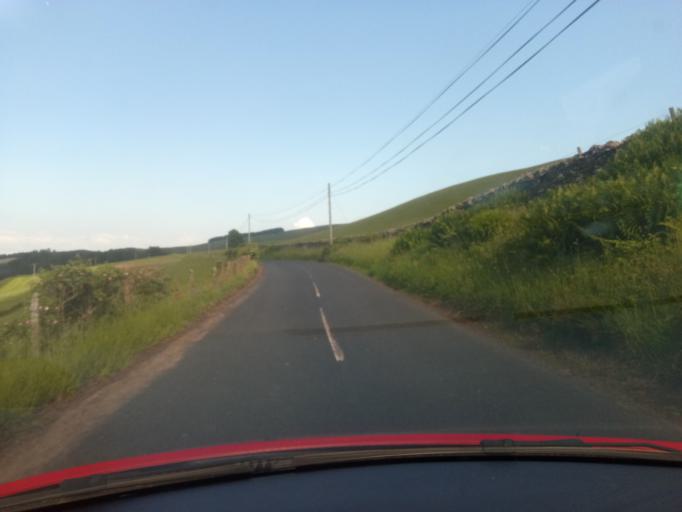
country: GB
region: Scotland
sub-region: The Scottish Borders
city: Selkirk
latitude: 55.5099
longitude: -2.9518
